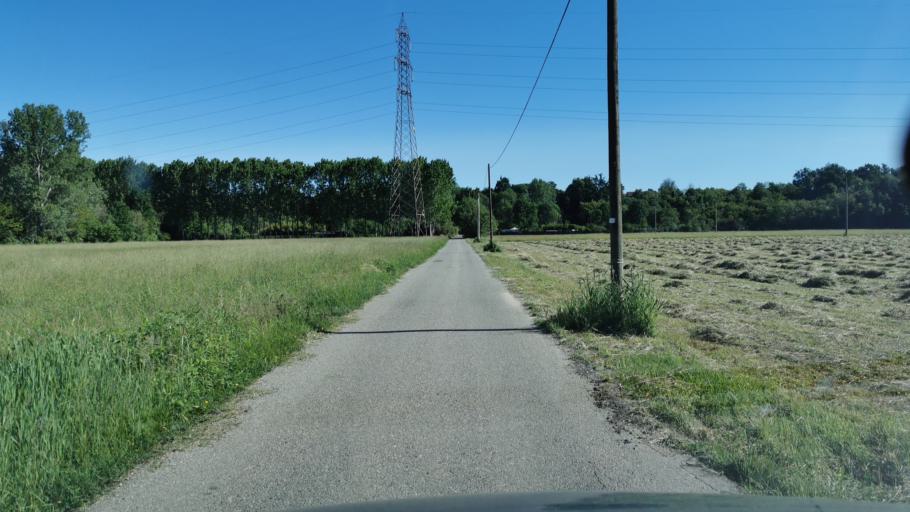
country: IT
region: Piedmont
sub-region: Provincia di Torino
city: Volpiano
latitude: 45.2013
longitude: 7.7463
